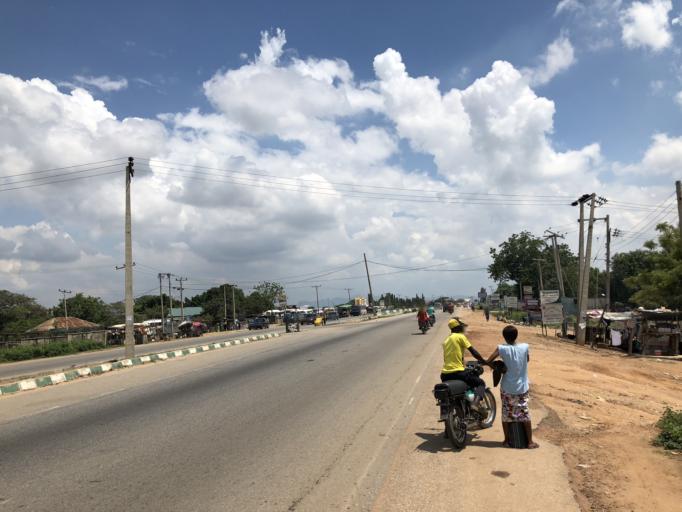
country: NG
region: Nassarawa
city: Karu
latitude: 8.9846
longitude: 7.6757
